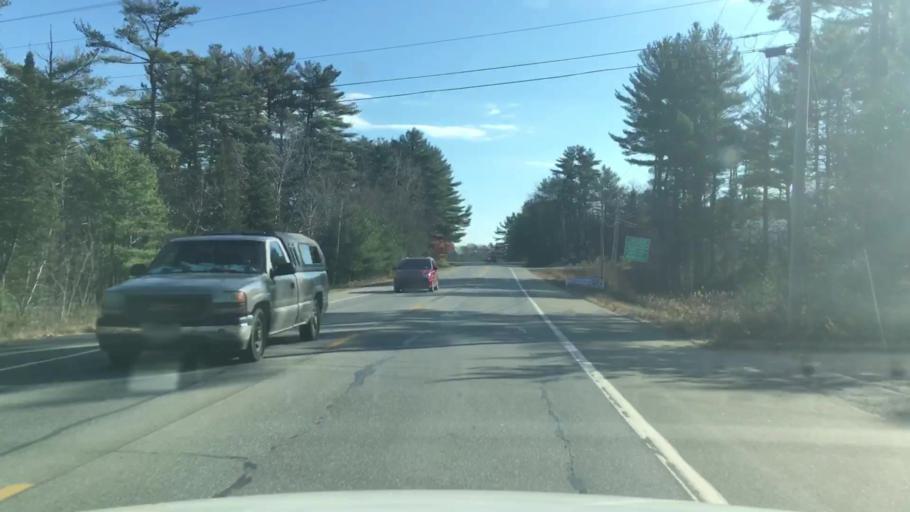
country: US
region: Maine
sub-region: Kennebec County
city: Windsor
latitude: 44.2629
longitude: -69.5594
